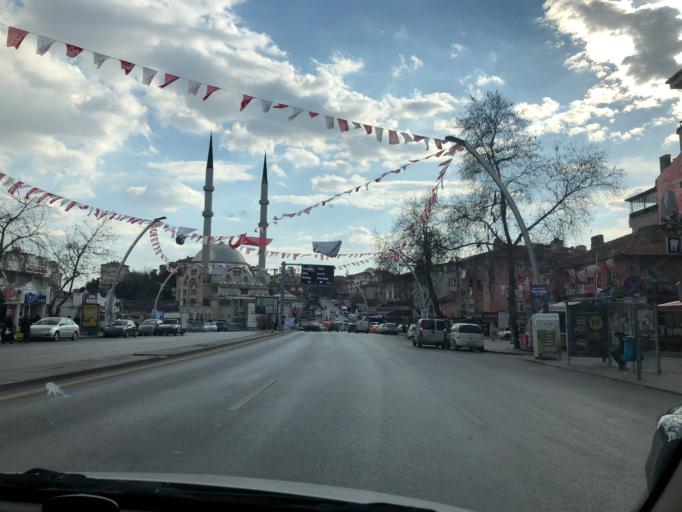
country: TR
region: Ankara
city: Mamak
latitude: 39.9855
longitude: 32.8639
